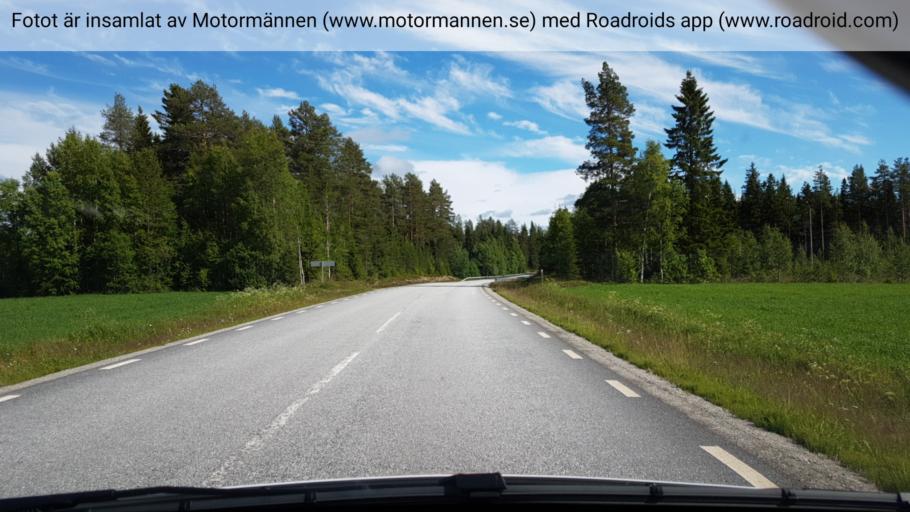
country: SE
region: Vaesterbotten
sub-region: Vindelns Kommun
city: Vindeln
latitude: 64.1048
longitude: 19.5959
